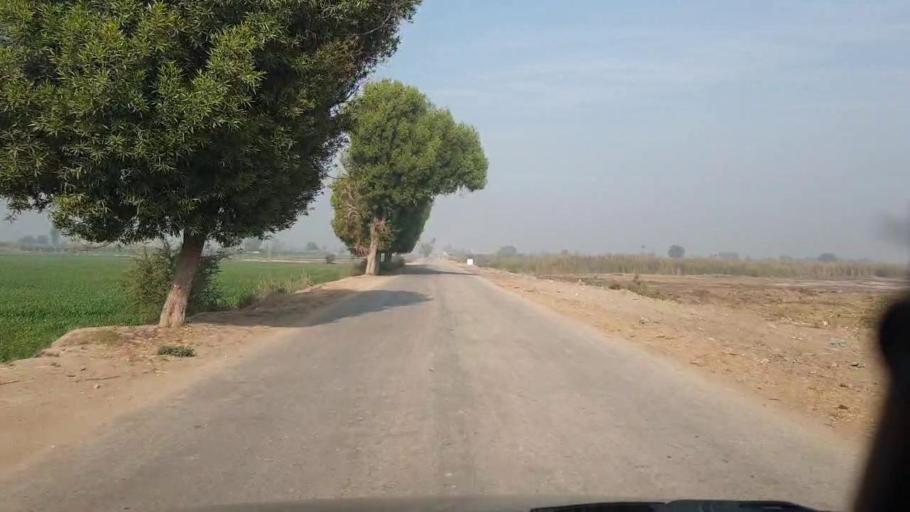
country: PK
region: Sindh
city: Shahdadpur
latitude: 25.9426
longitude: 68.6004
